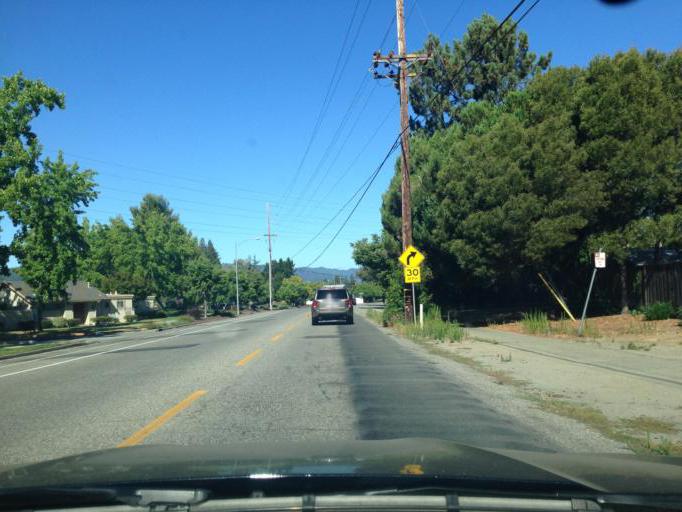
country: US
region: California
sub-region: Santa Clara County
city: Cambrian Park
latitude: 37.2434
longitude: -121.9440
